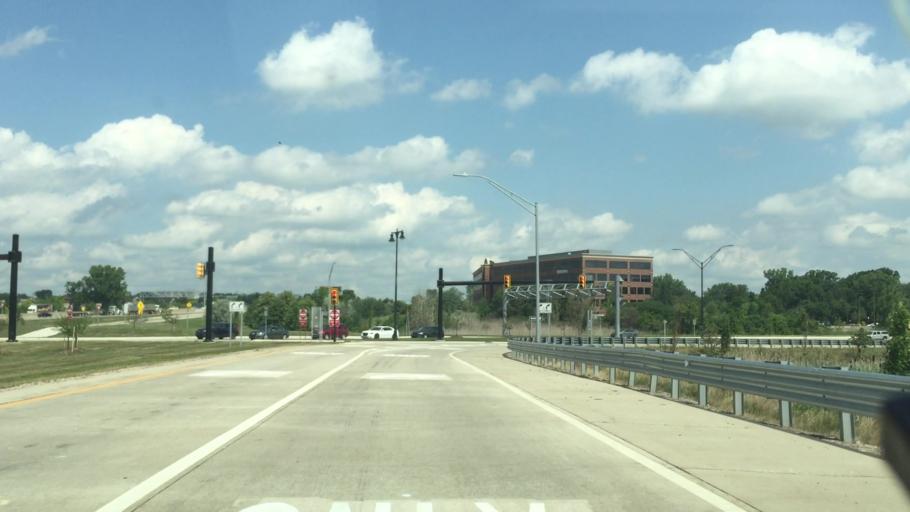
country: US
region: Michigan
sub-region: Oakland County
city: Auburn Hills
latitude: 42.6665
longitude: -83.2388
